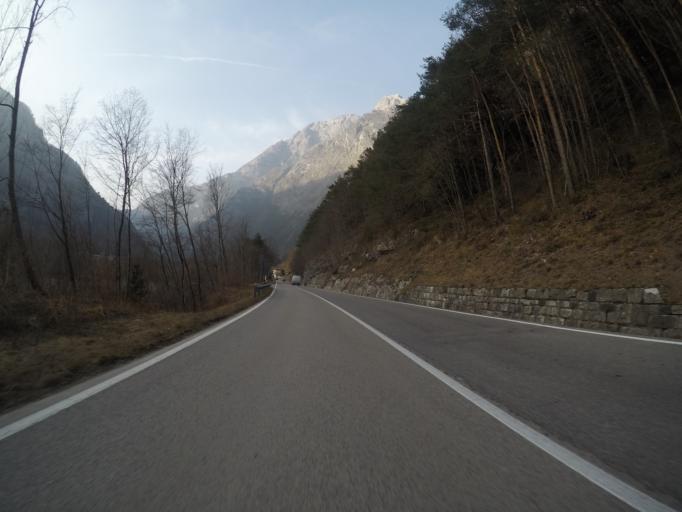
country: IT
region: Veneto
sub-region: Provincia di Belluno
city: La Valle Agordina
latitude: 46.2428
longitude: 12.1065
